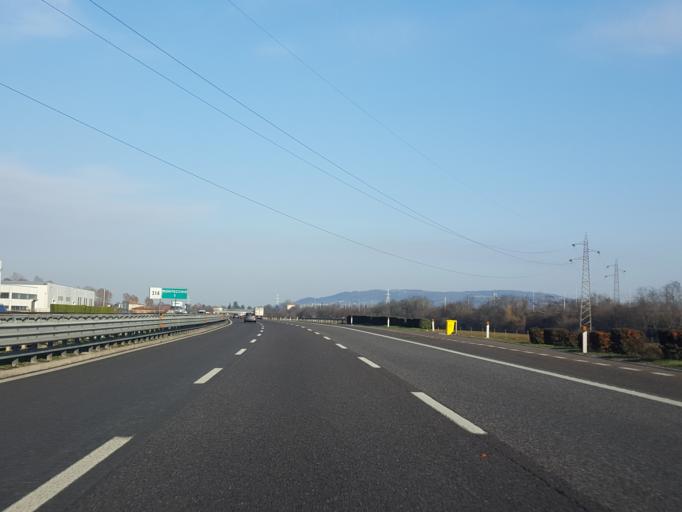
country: IT
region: Veneto
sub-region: Provincia di Vicenza
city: Montebello Vicentino
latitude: 45.4450
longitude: 11.3790
